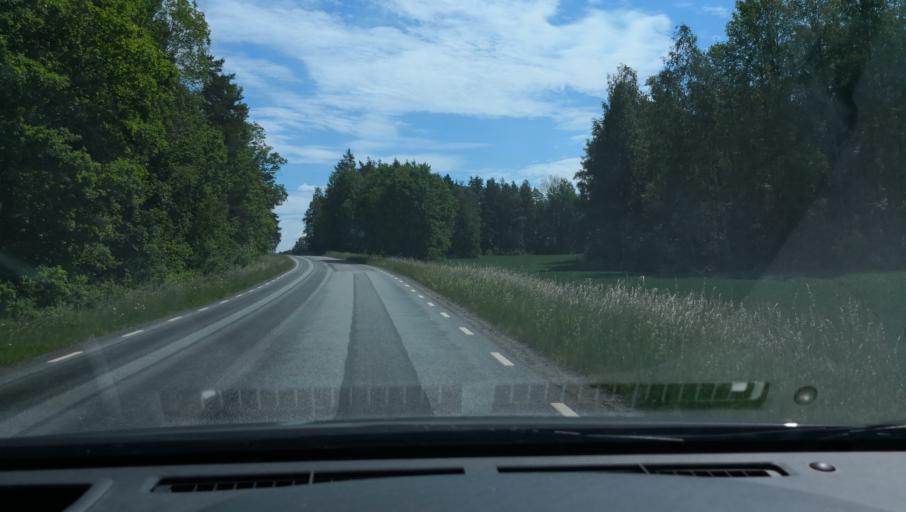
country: SE
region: Uppsala
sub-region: Habo Kommun
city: Balsta
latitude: 59.6564
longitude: 17.4544
